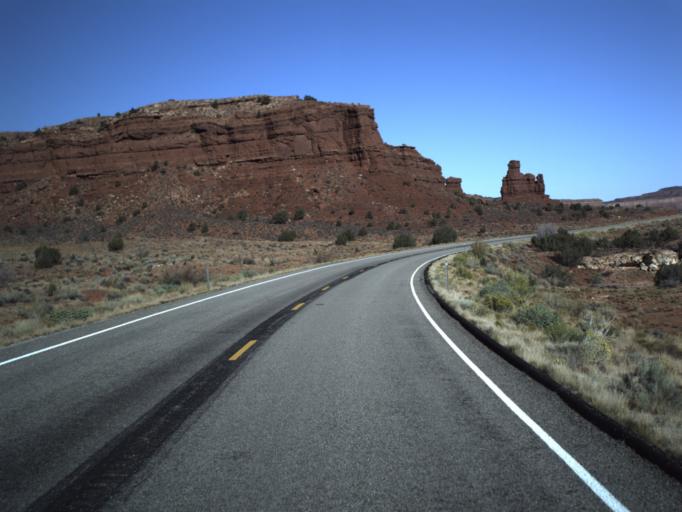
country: US
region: Utah
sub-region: San Juan County
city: Blanding
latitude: 37.6929
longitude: -110.2288
